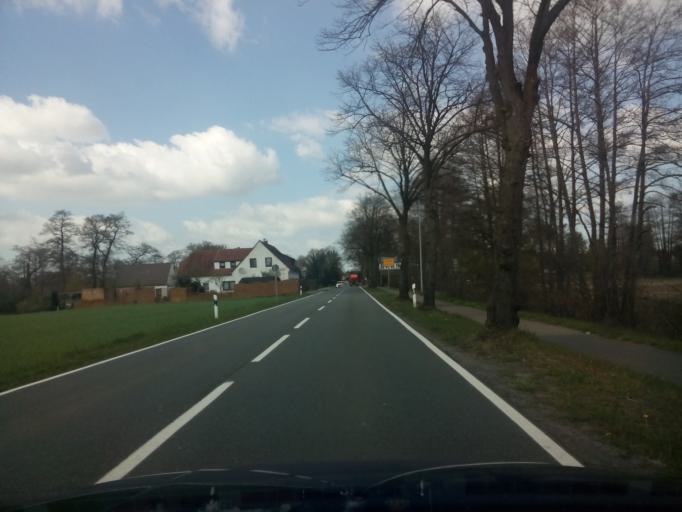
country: DE
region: Lower Saxony
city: Lilienthal
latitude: 53.1662
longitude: 8.9276
